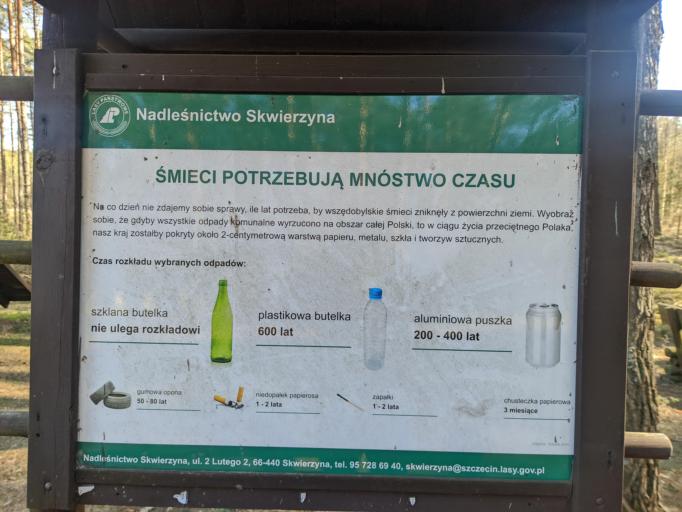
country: PL
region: Lubusz
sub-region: Powiat miedzyrzecki
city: Bledzew
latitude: 52.5882
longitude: 15.4271
